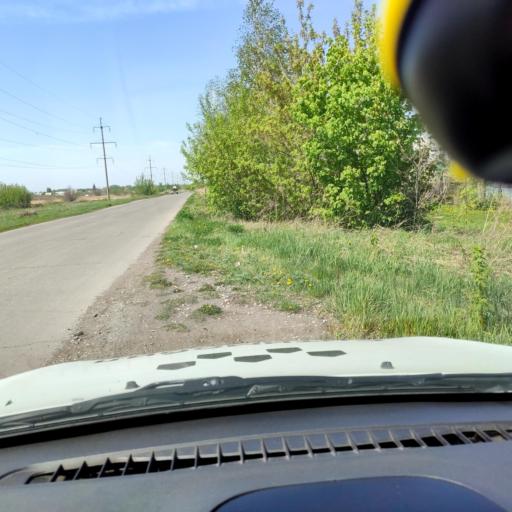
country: RU
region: Samara
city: Tol'yatti
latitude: 53.6630
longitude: 49.3613
